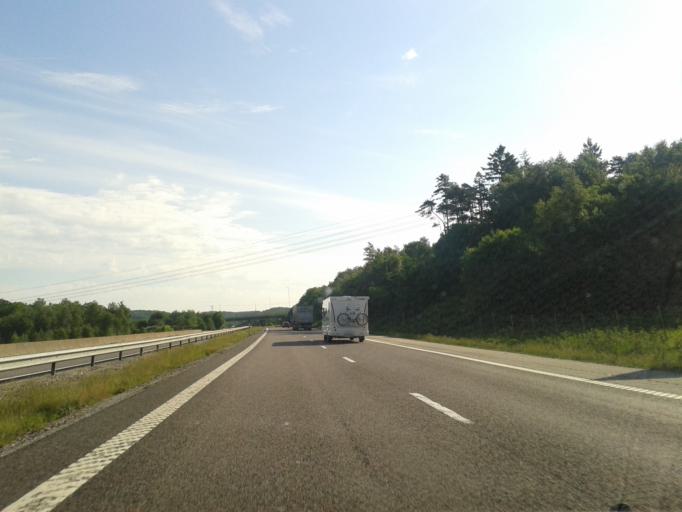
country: SE
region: Vaestra Goetaland
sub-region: Stenungsunds Kommun
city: Stora Hoga
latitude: 58.0536
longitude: 11.8723
